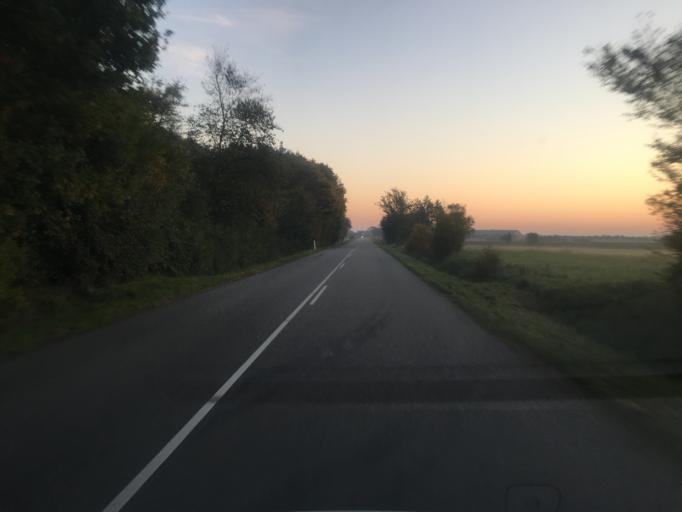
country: DK
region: South Denmark
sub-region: Aabenraa Kommune
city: Tinglev
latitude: 54.9706
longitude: 9.1247
